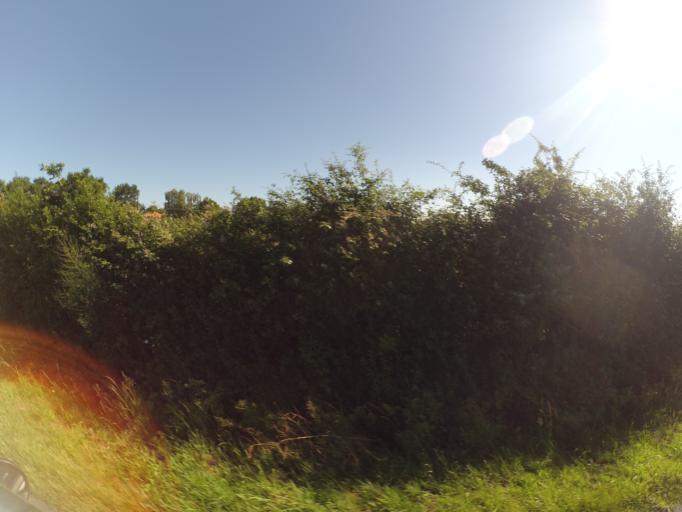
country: FR
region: Pays de la Loire
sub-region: Departement de la Vendee
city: Beaurepaire
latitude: 46.8949
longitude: -1.0583
